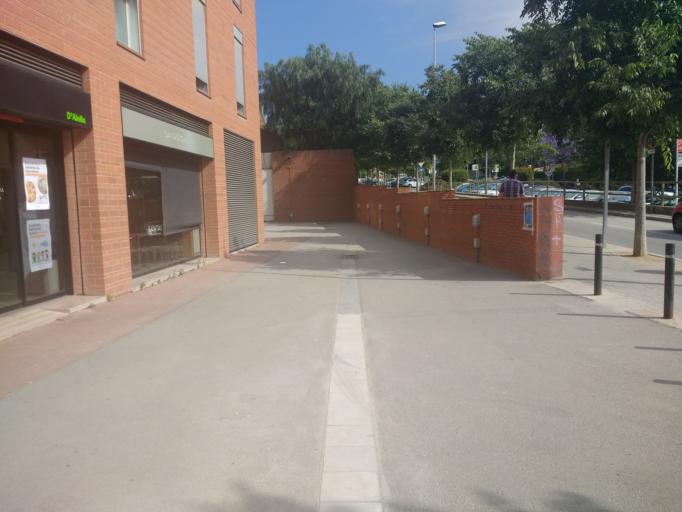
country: ES
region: Catalonia
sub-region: Provincia de Barcelona
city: Alella
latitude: 41.4907
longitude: 2.2959
